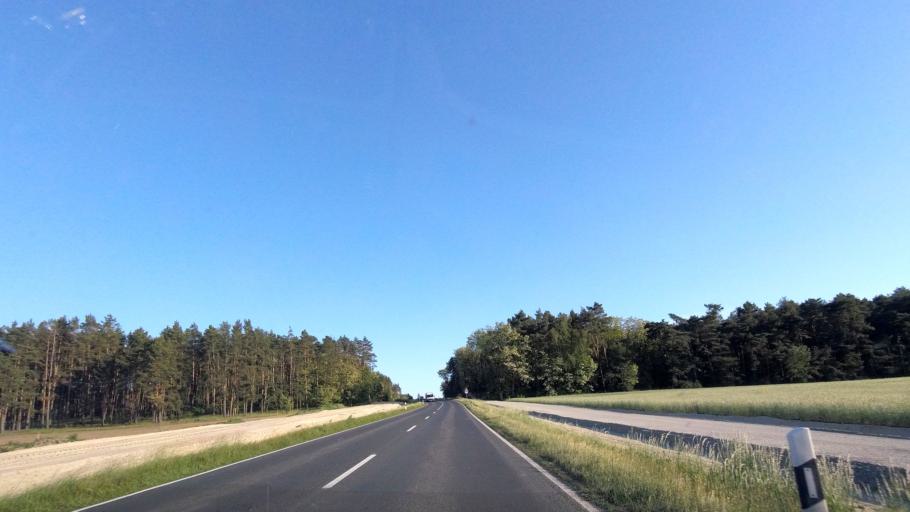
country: DE
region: Brandenburg
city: Brandenburg an der Havel
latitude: 52.3580
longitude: 12.5977
